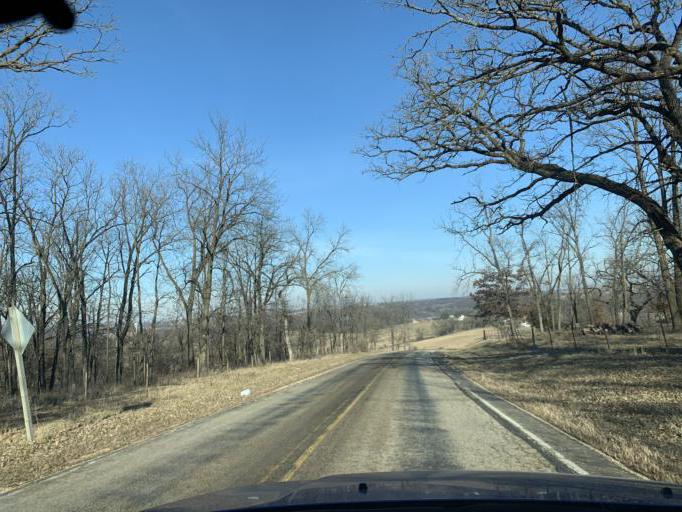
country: US
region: Wisconsin
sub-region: Iowa County
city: Barneveld
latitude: 42.8623
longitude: -89.9398
